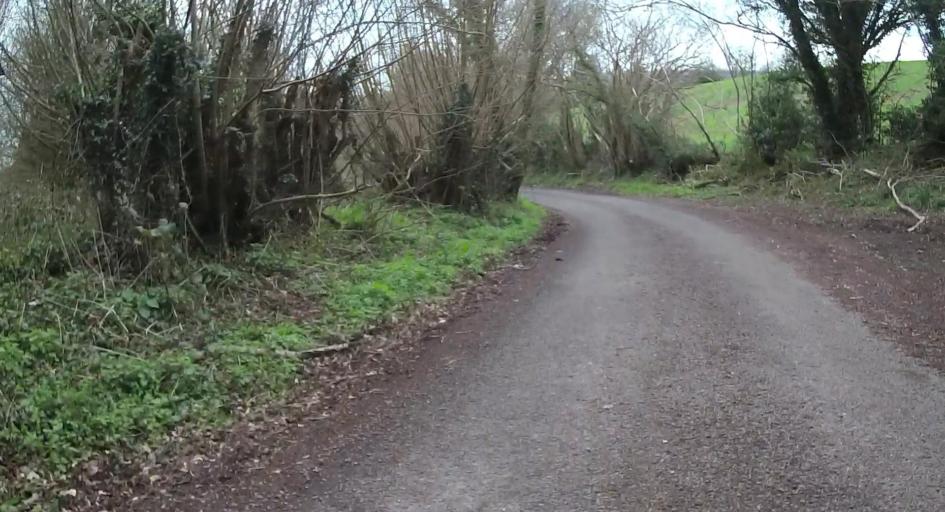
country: GB
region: England
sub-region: Hampshire
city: Alton
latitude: 51.1676
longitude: -0.9746
